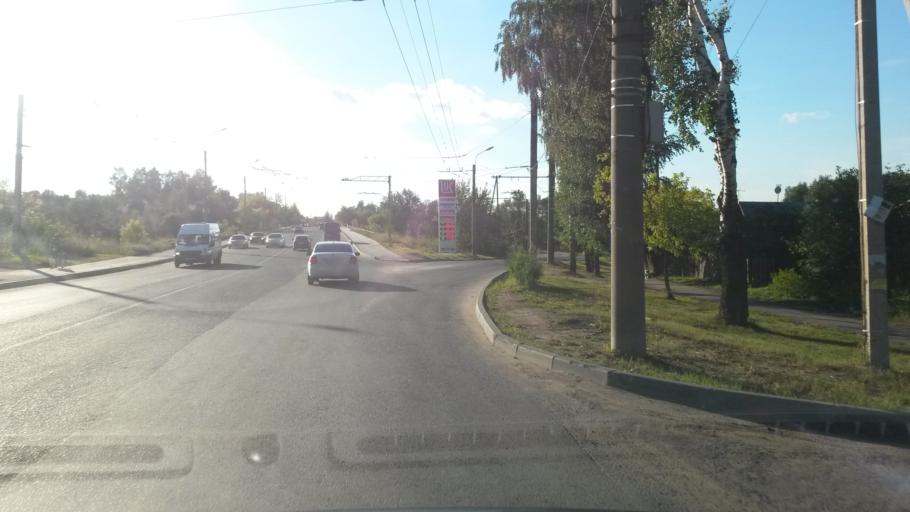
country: RU
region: Ivanovo
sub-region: Gorod Ivanovo
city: Ivanovo
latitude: 57.0160
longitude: 40.9289
